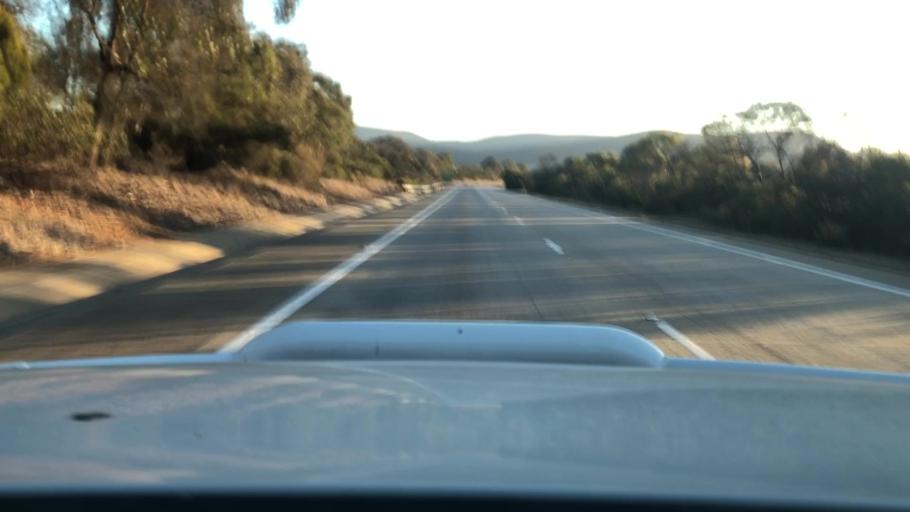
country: AU
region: New South Wales
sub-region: Goulburn Mulwaree
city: Goulburn
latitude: -34.7489
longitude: 149.7690
